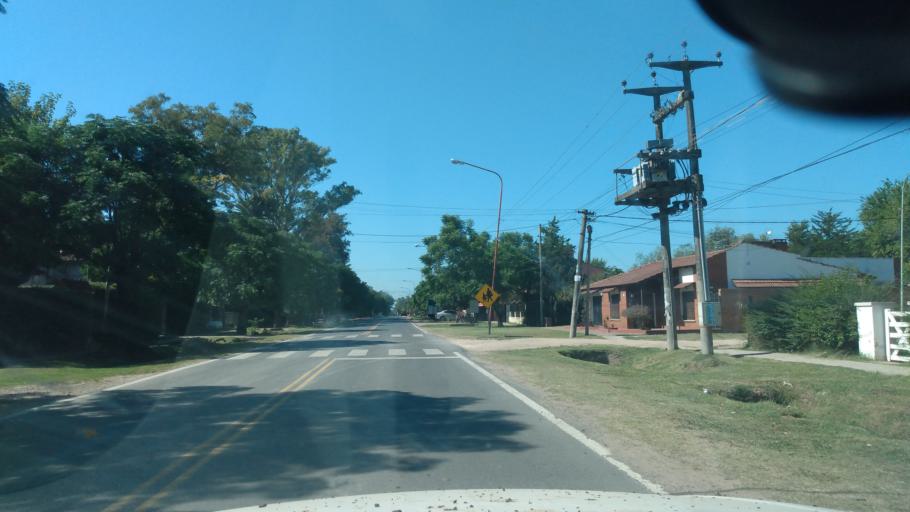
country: AR
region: Buenos Aires
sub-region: Partido de Lujan
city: Lujan
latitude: -34.4922
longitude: -59.0768
